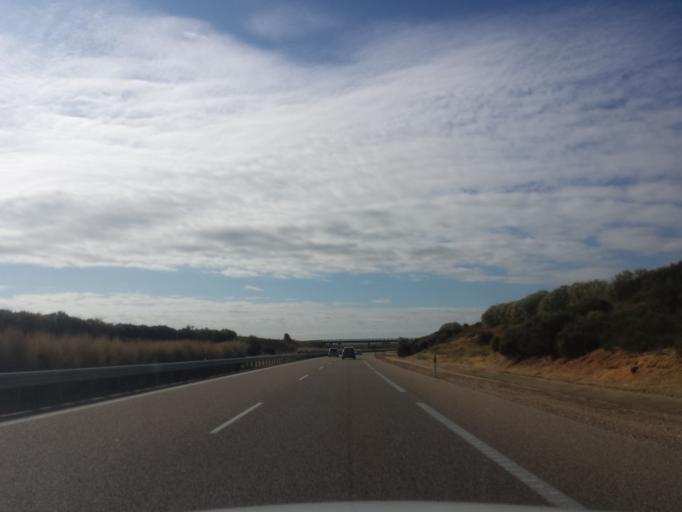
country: ES
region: Castille and Leon
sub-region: Provincia de Leon
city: Villamanan
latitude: 42.3074
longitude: -5.5955
